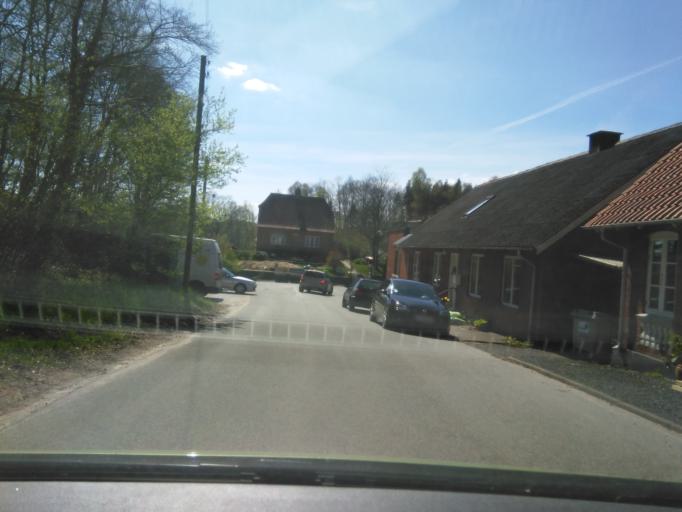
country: DK
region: Central Jutland
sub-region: Viborg Kommune
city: Viborg
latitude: 56.3713
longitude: 9.3203
